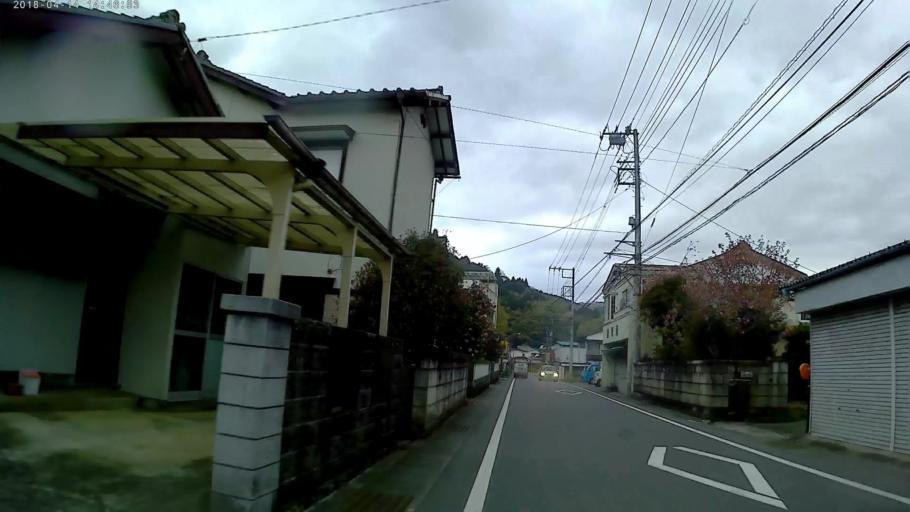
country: JP
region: Shizuoka
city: Gotemba
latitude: 35.3650
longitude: 138.9842
